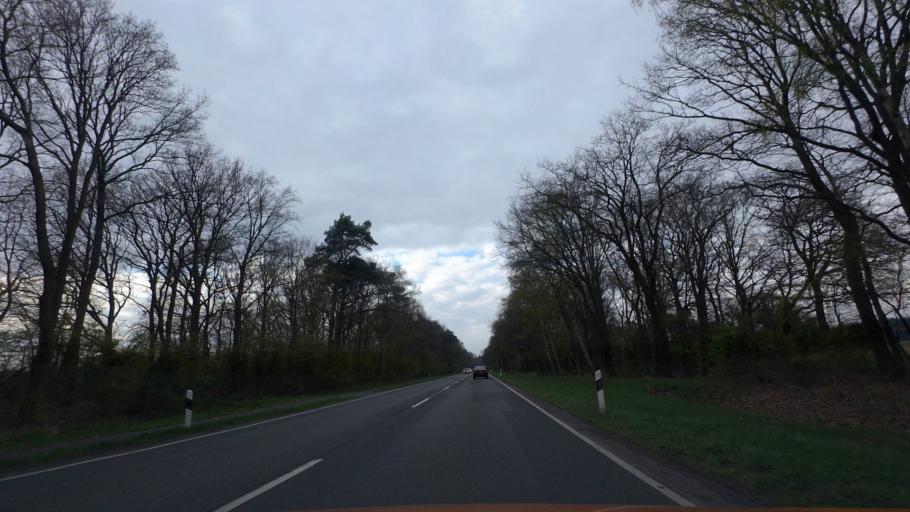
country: DE
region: Lower Saxony
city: Molbergen
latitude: 52.9307
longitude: 7.9484
